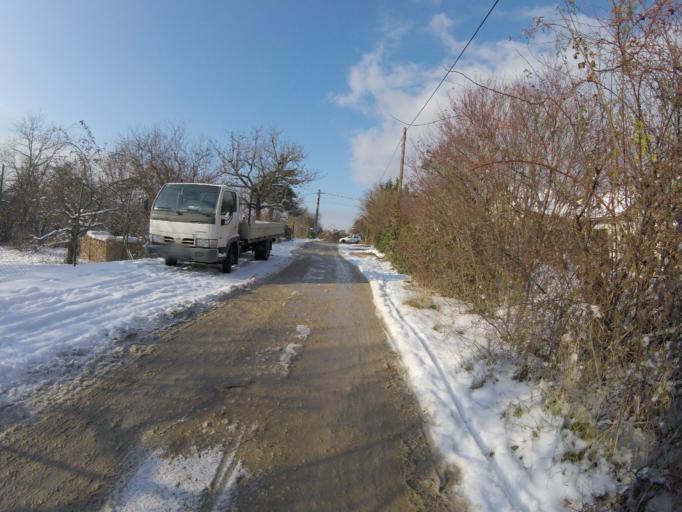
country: HU
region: Pest
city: Budakeszi
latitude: 47.5054
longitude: 18.9269
